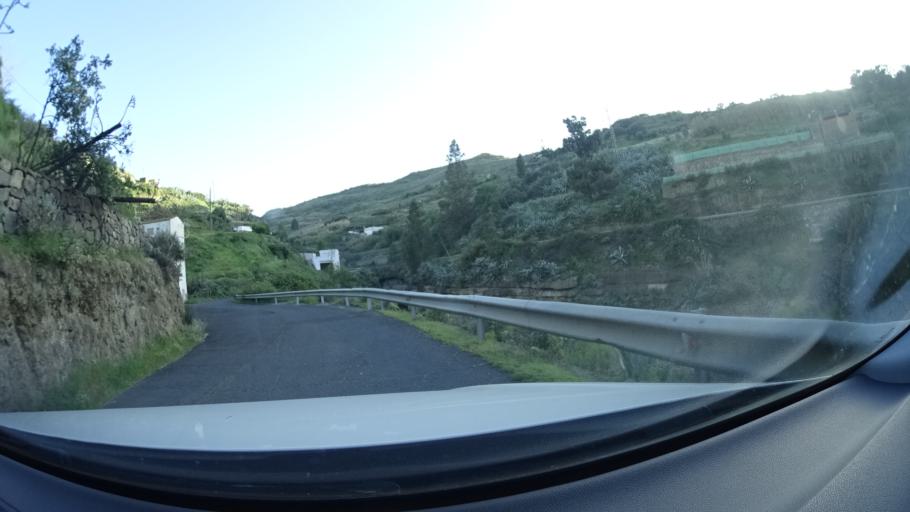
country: ES
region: Canary Islands
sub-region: Provincia de Las Palmas
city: Artenara
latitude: 28.0440
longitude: -15.6711
